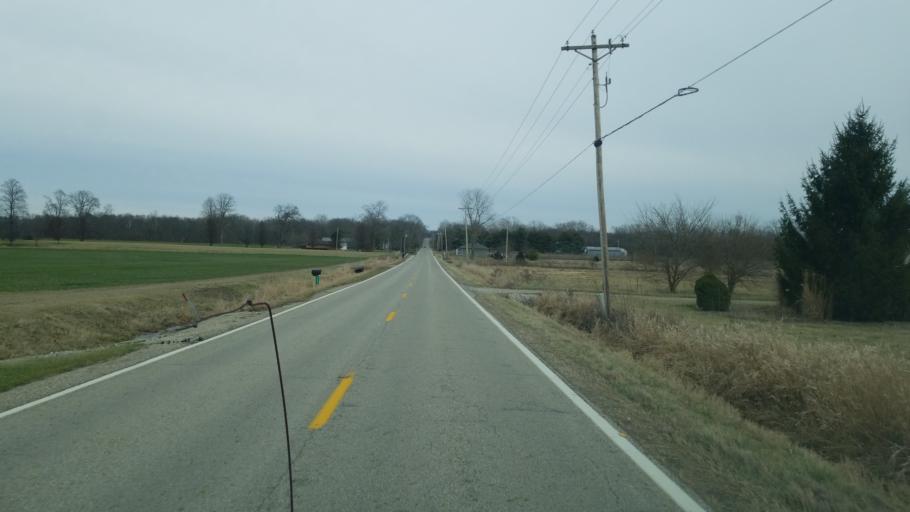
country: US
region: Ohio
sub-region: Pickaway County
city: Williamsport
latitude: 39.5503
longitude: -83.1138
